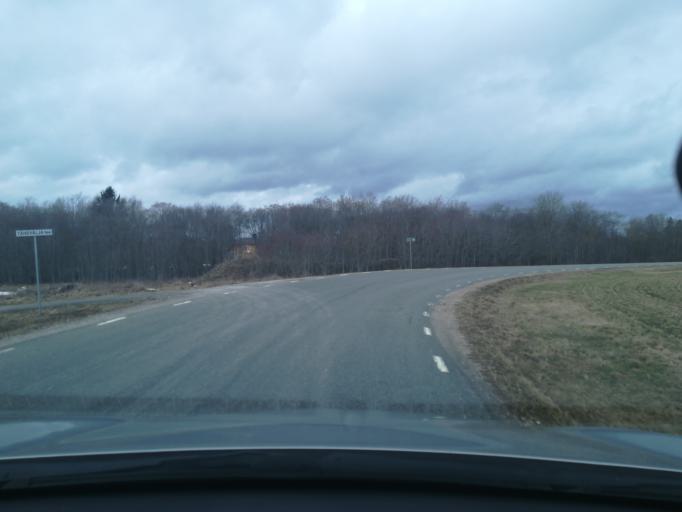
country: EE
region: Harju
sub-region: Saue linn
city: Saue
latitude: 59.3481
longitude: 24.5386
